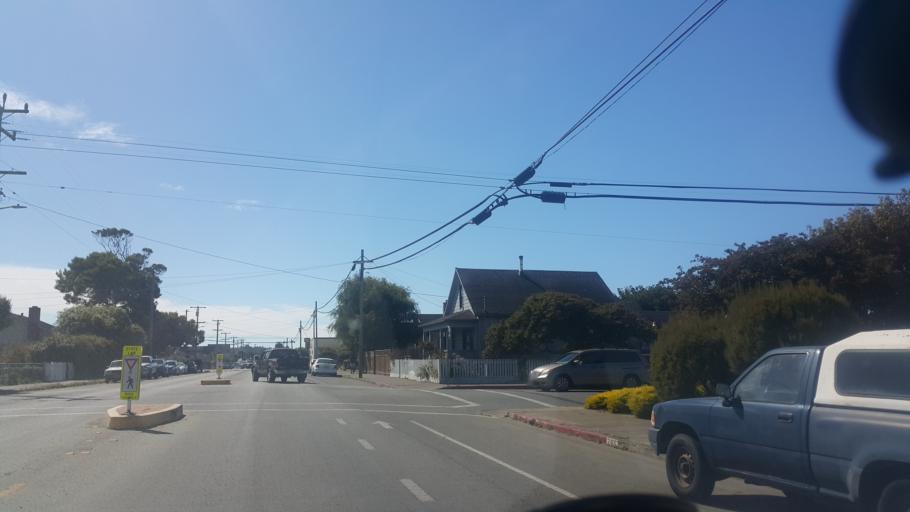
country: US
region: California
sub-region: Mendocino County
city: Fort Bragg
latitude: 39.4432
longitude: -123.7981
